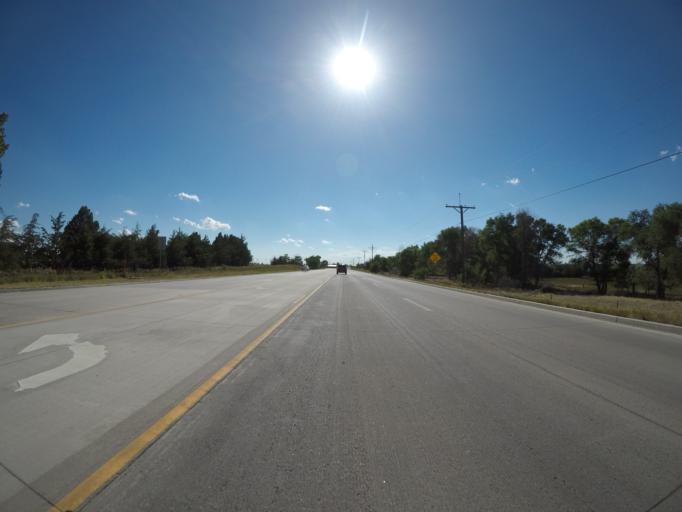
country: US
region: Colorado
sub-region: Logan County
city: Sterling
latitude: 40.6240
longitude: -103.2541
